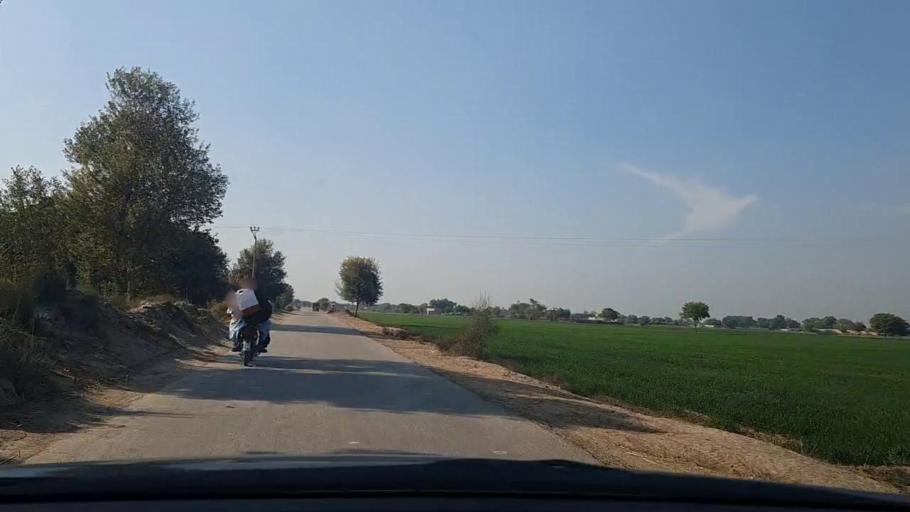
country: PK
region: Sindh
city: Daulatpur
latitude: 26.3121
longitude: 68.0738
